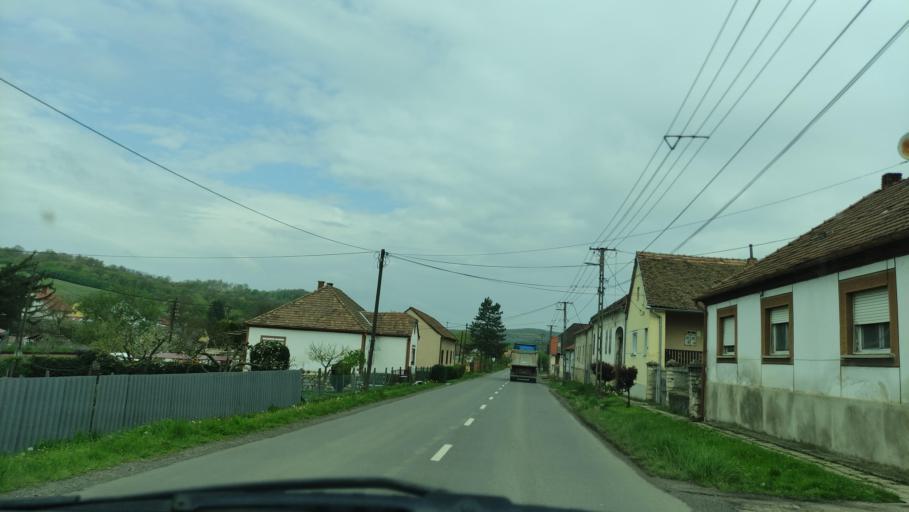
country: HU
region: Baranya
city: Komlo
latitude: 46.2130
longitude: 18.2435
